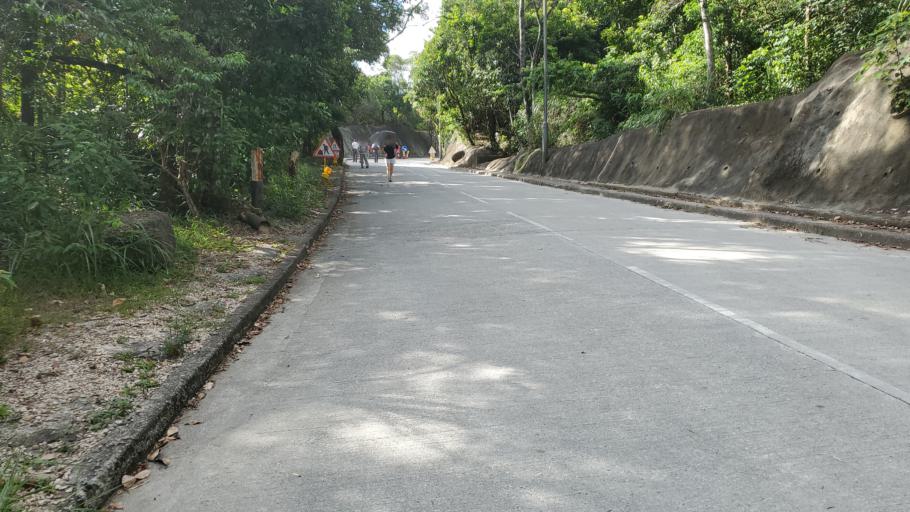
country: HK
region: Sai Kung
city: Sai Kung
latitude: 22.3949
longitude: 114.2310
